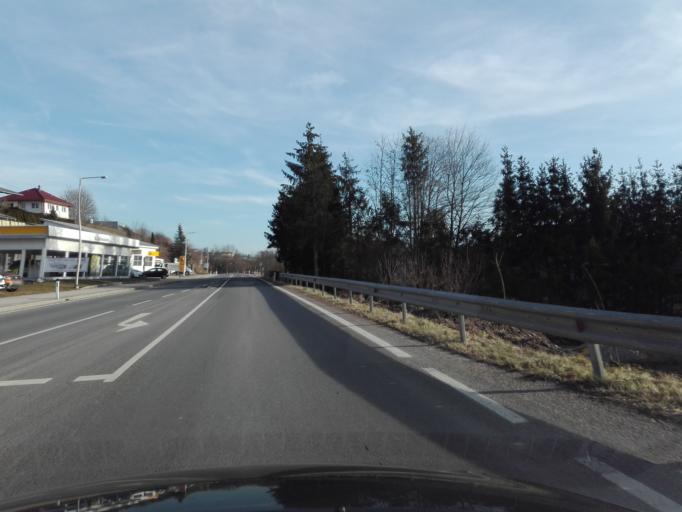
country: AT
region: Lower Austria
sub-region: Politischer Bezirk Amstetten
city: Zeillern
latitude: 48.1750
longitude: 14.8300
